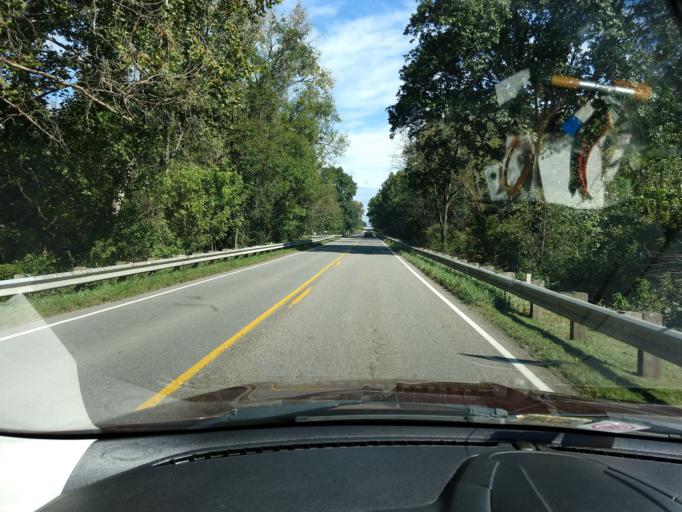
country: US
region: Virginia
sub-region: Augusta County
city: Crimora
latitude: 38.1847
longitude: -78.8420
